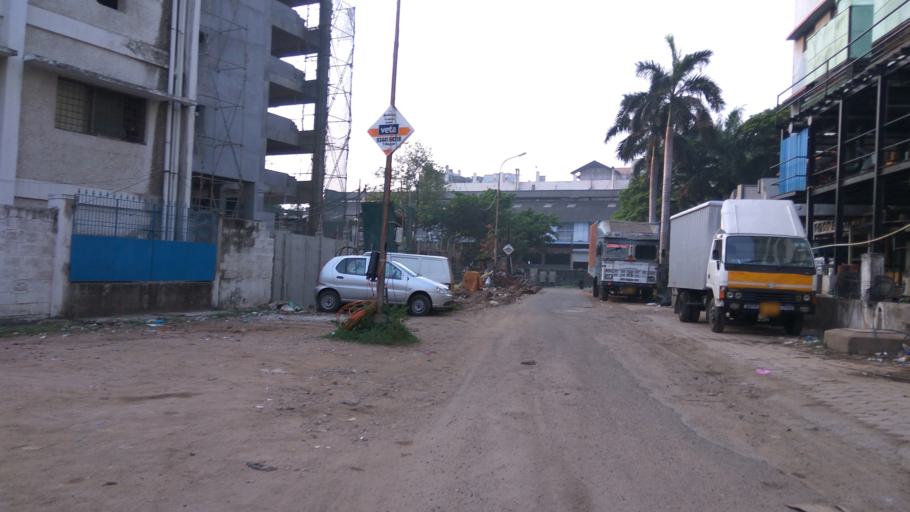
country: IN
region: Tamil Nadu
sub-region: Kancheepuram
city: Alandur
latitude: 13.0138
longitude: 80.2102
